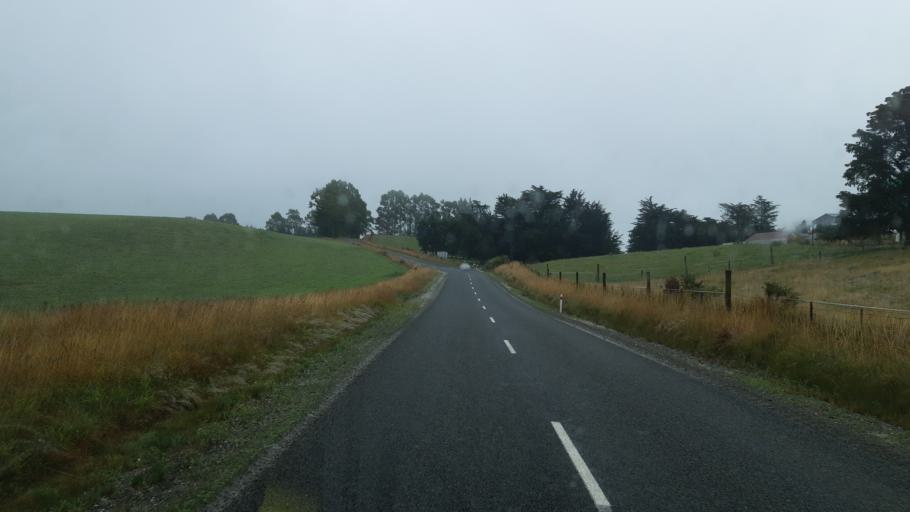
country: NZ
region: Otago
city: Oamaru
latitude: -44.9383
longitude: 170.7465
